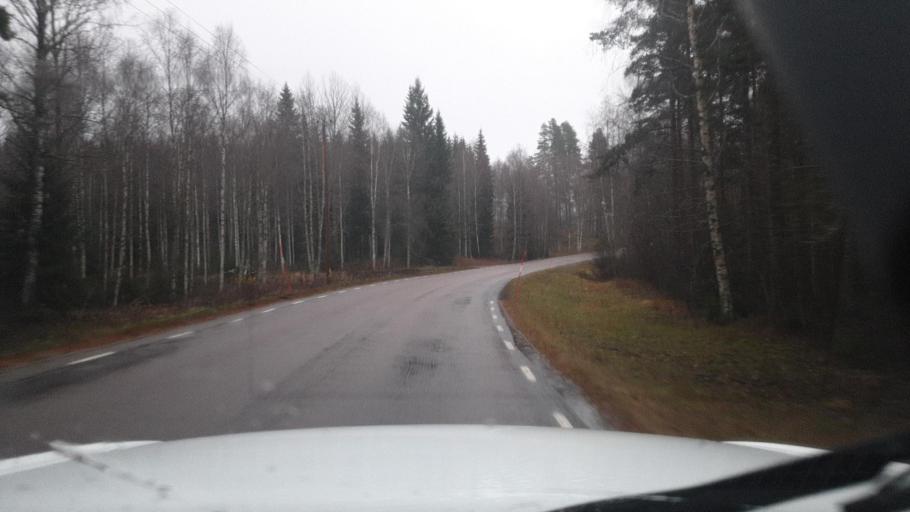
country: SE
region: Vaermland
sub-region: Arvika Kommun
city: Arvika
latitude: 59.9563
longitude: 12.7162
